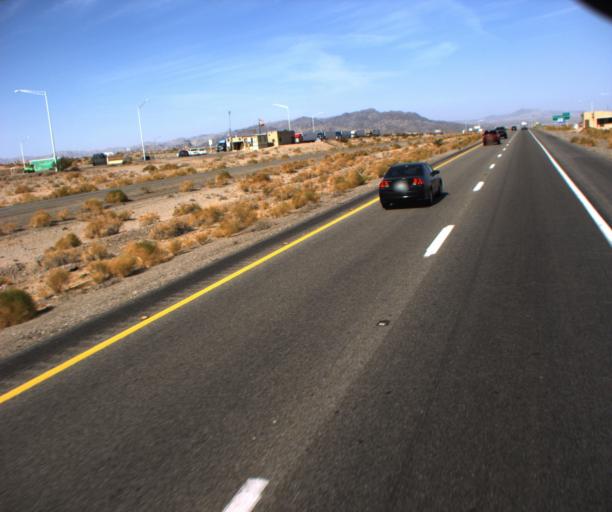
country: US
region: Arizona
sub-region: Mohave County
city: Desert Hills
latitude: 34.7242
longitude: -114.4188
